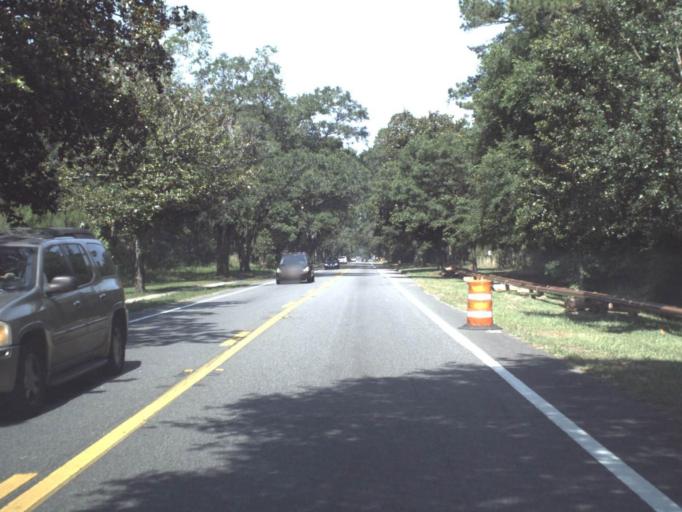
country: US
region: Florida
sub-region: Clay County
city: Asbury Lake
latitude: 29.9826
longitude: -81.8007
